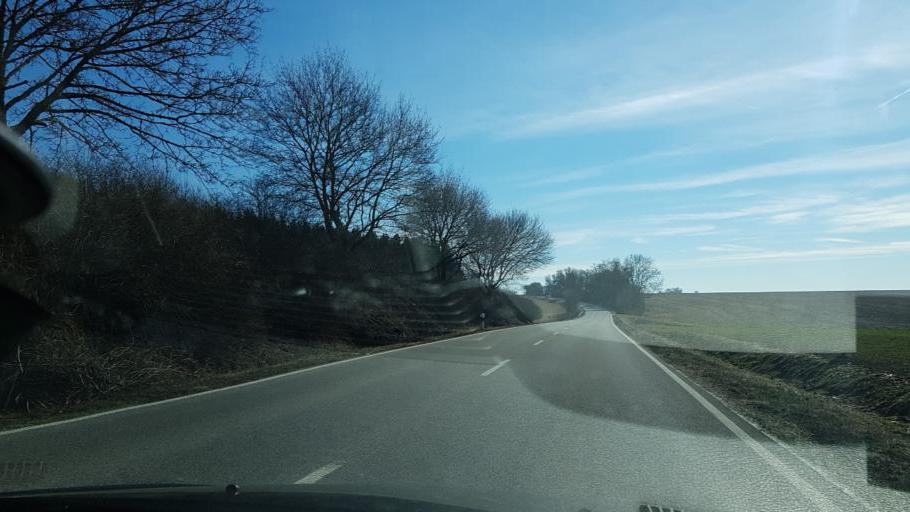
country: DE
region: Bavaria
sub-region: Upper Bavaria
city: Mittelstetten
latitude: 48.2388
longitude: 11.1061
